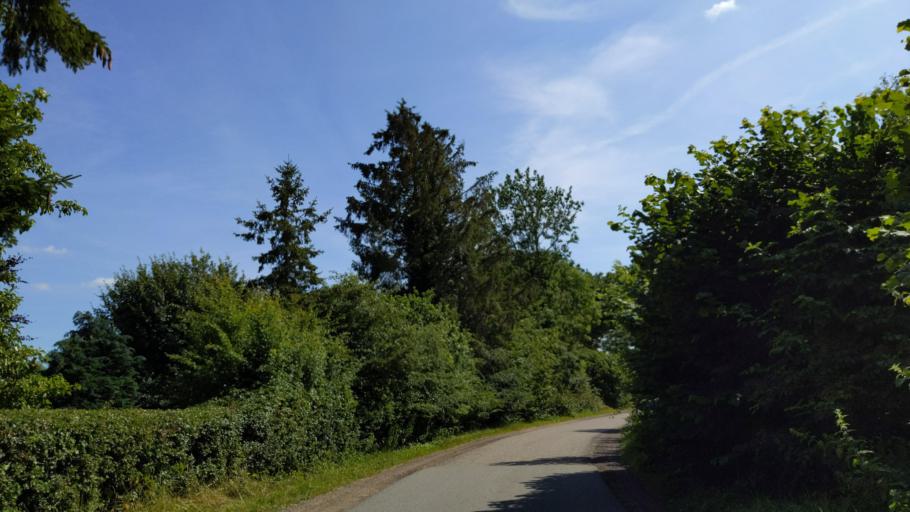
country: DE
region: Schleswig-Holstein
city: Altenkrempe
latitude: 54.1528
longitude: 10.8339
